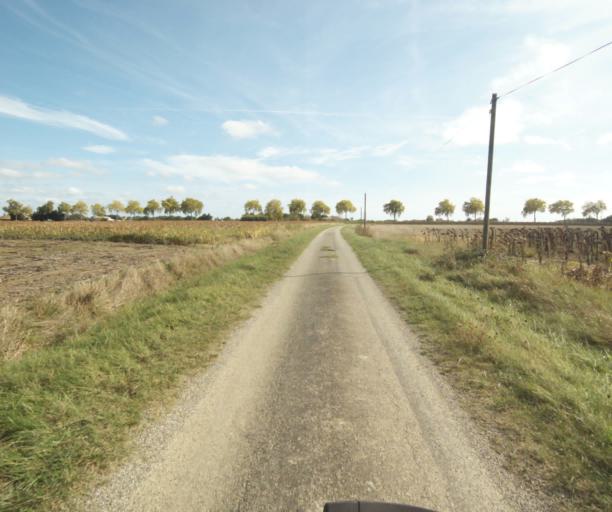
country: FR
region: Midi-Pyrenees
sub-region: Departement du Tarn-et-Garonne
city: Saint-Porquier
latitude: 43.9466
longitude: 1.1426
